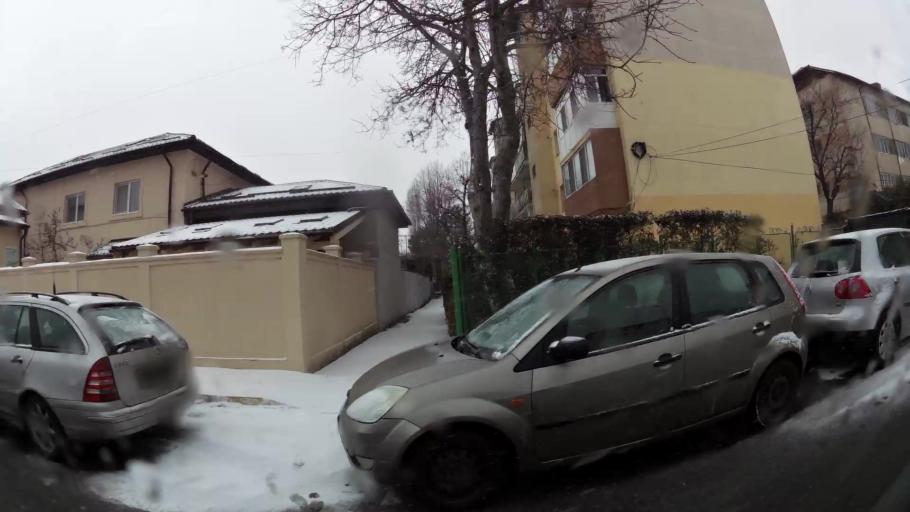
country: RO
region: Dambovita
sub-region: Municipiul Targoviste
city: Targoviste
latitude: 44.9288
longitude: 25.4491
